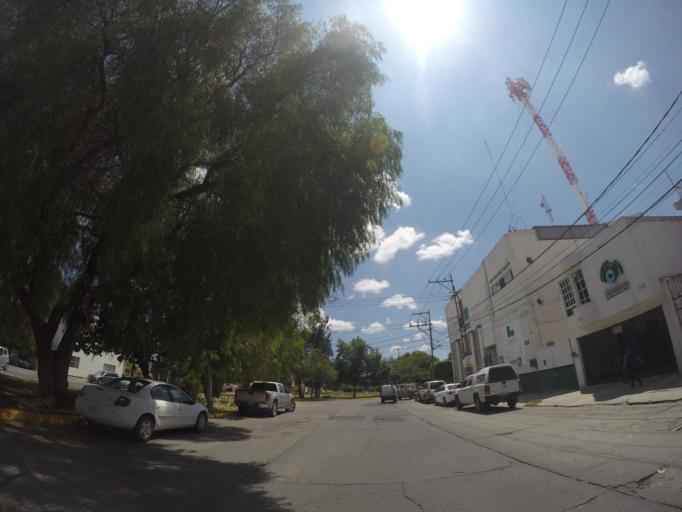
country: MX
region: San Luis Potosi
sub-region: San Luis Potosi
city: San Luis Potosi
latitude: 22.1412
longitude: -100.9931
